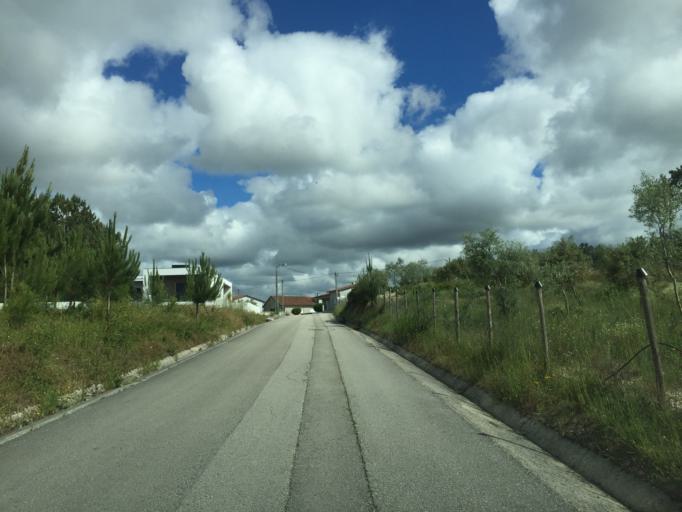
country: PT
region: Leiria
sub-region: Pombal
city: Lourical
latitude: 39.9796
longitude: -8.8034
